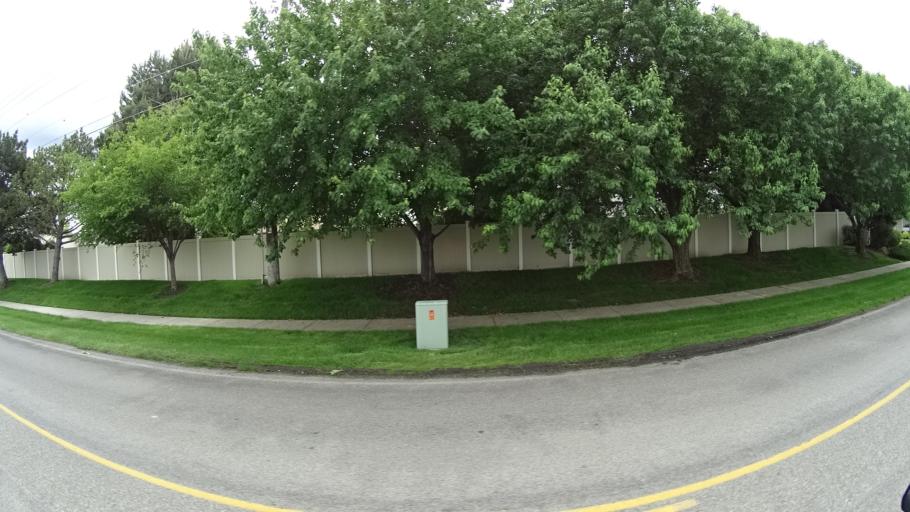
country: US
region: Idaho
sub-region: Ada County
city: Meridian
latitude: 43.6340
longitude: -116.4264
